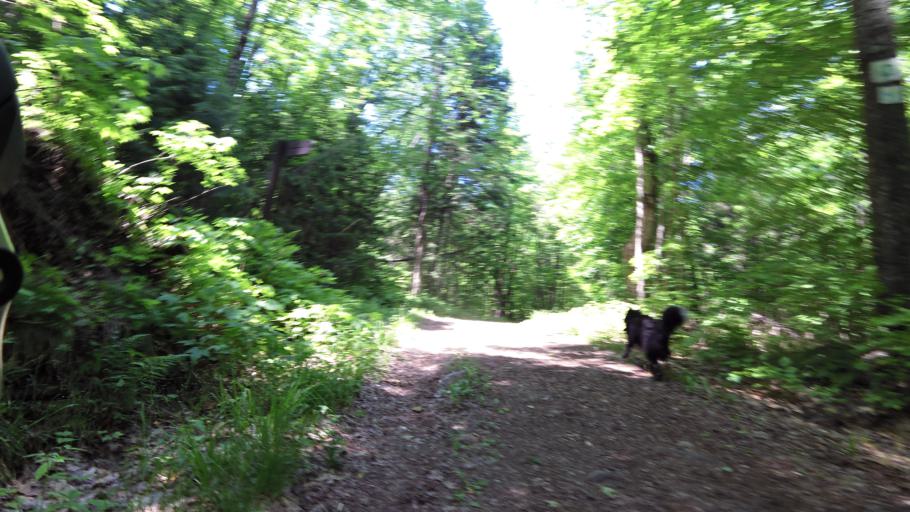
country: CA
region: Quebec
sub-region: Outaouais
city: Wakefield
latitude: 45.5675
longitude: -75.9296
